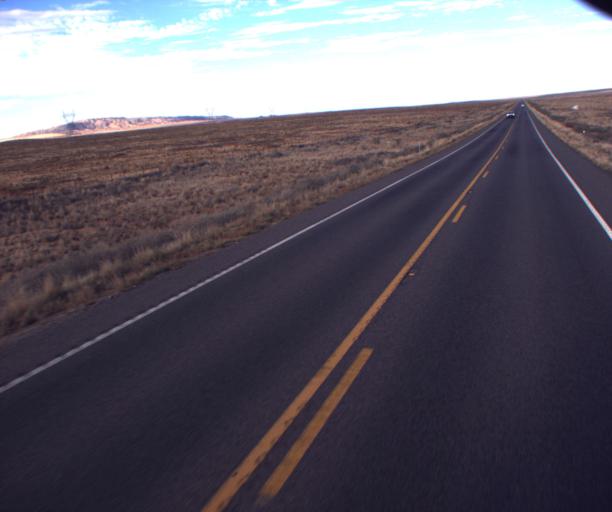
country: US
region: Arizona
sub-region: Apache County
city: Lukachukai
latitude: 36.9396
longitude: -109.2482
